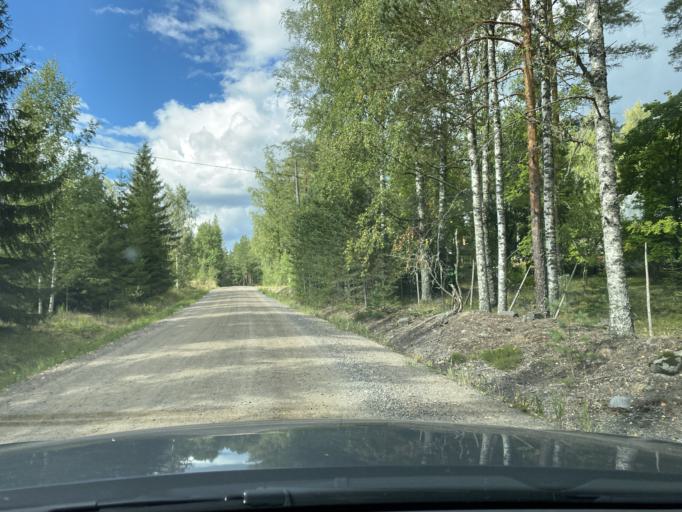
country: FI
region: Haeme
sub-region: Forssa
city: Humppila
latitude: 61.0773
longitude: 23.2745
